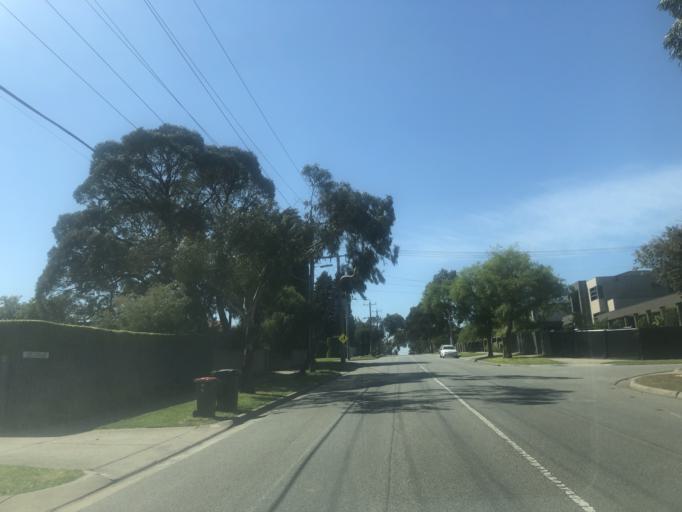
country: AU
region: Victoria
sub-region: Monash
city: Mulgrave
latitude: -37.9019
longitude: 145.1804
